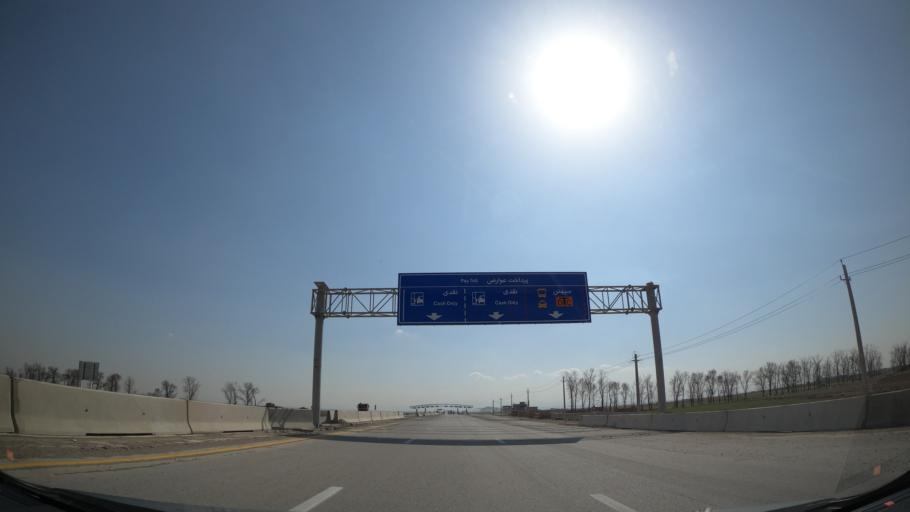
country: IR
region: Qazvin
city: Abyek
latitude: 35.9626
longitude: 50.4632
